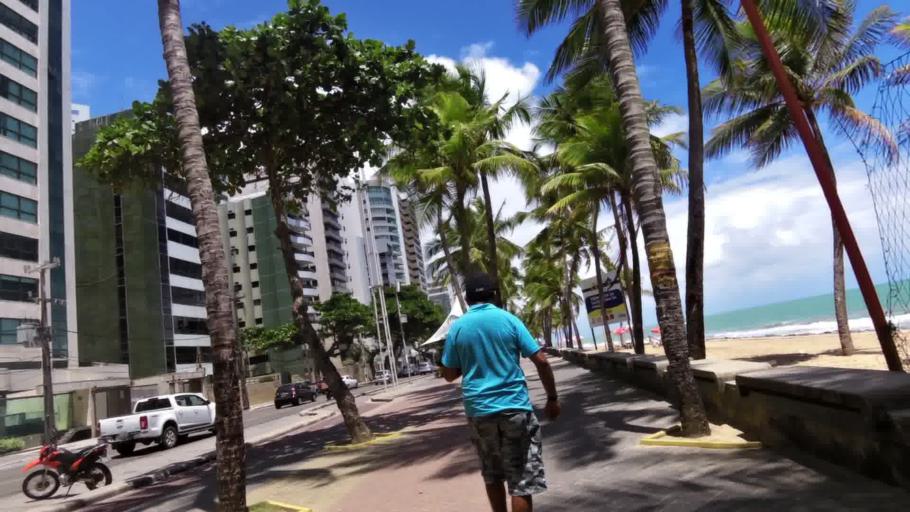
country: BR
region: Pernambuco
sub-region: Recife
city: Recife
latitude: -8.1446
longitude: -34.9048
